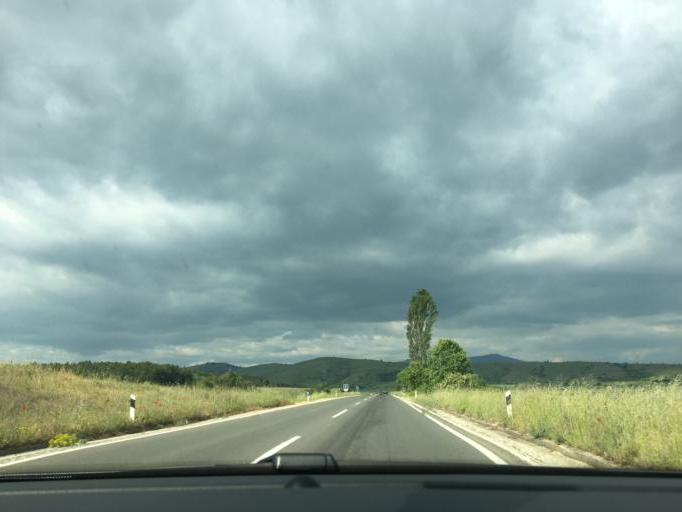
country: MK
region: Prilep
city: Topolcani
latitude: 41.2651
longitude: 21.4685
